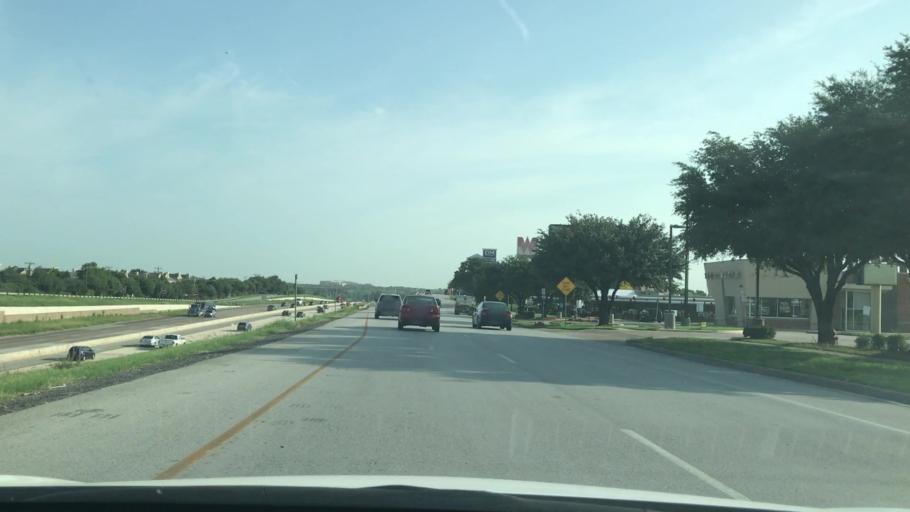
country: US
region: Texas
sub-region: Tarrant County
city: Euless
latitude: 32.7937
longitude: -97.0564
